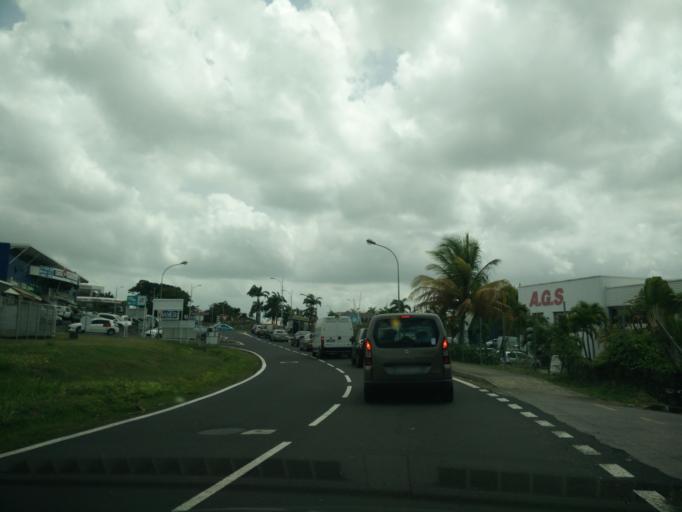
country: GP
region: Guadeloupe
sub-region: Guadeloupe
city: Baie-Mahault
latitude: 16.2395
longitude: -61.5829
